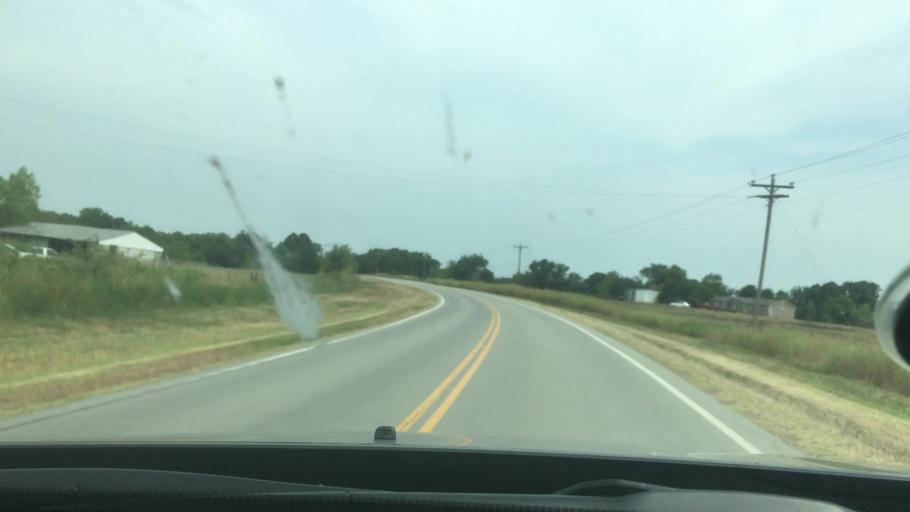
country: US
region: Oklahoma
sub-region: Coal County
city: Coalgate
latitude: 34.5783
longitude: -96.4075
